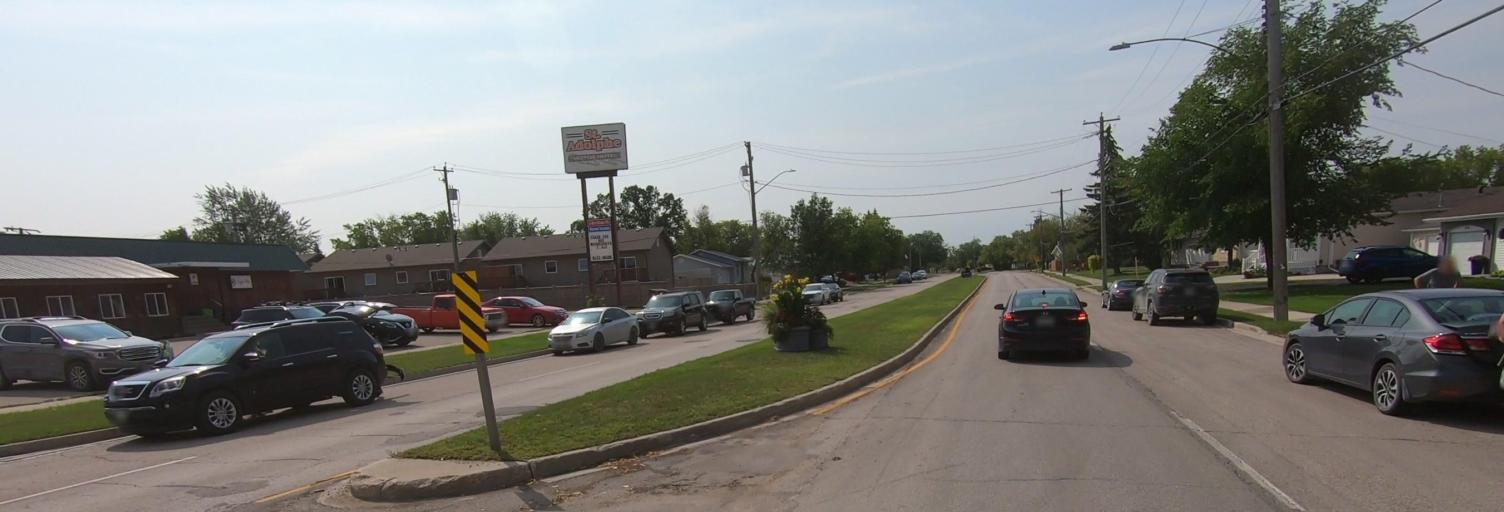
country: CA
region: Manitoba
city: Niverville
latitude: 49.6715
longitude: -97.1119
